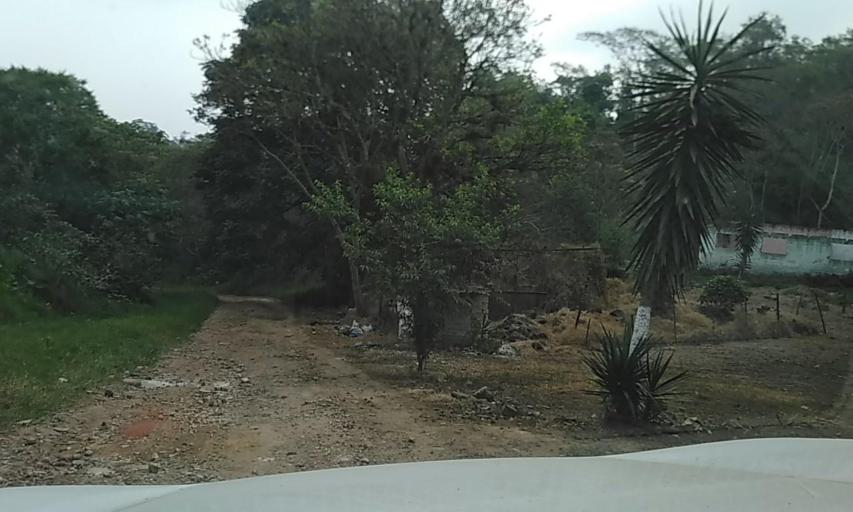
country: MX
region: Veracruz
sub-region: Xalapa
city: Lomas Verdes
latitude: 19.5025
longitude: -96.9156
